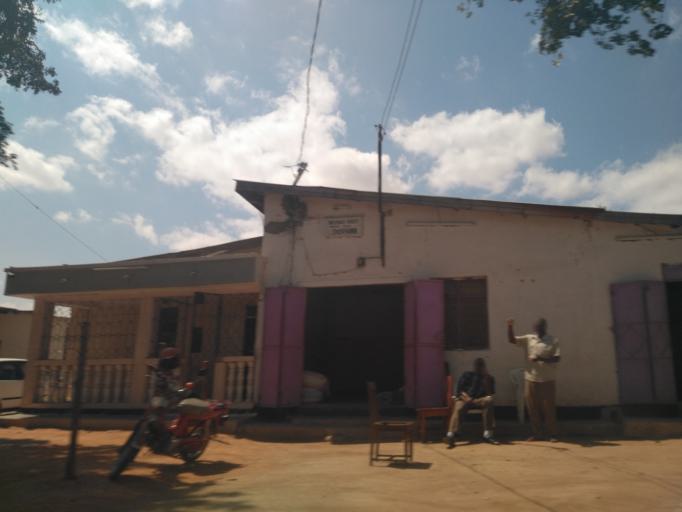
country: TZ
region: Dodoma
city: Dodoma
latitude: -6.1766
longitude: 35.7408
